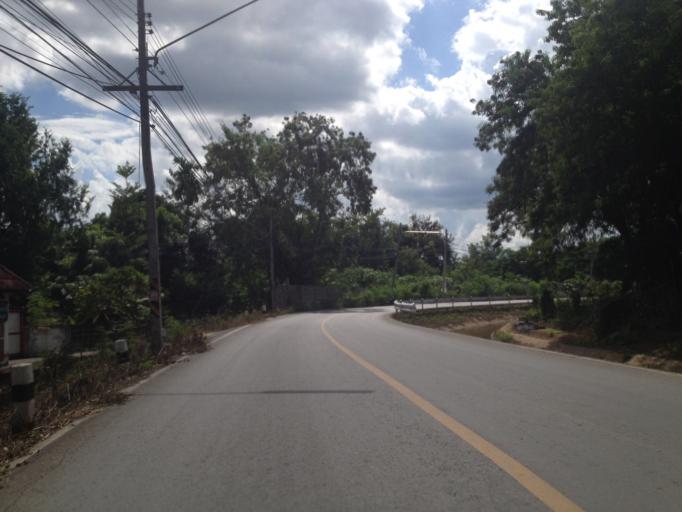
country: TH
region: Chiang Mai
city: Hang Dong
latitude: 18.7105
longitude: 98.9394
